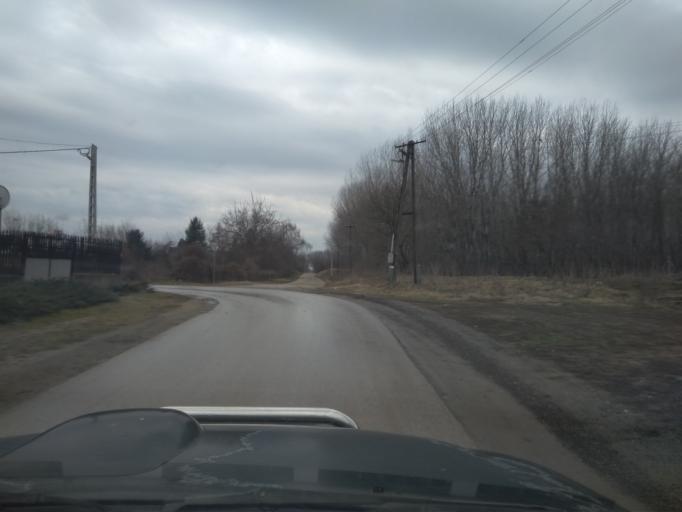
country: HU
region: Szabolcs-Szatmar-Bereg
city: Nyiregyhaza
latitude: 47.9654
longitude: 21.6852
